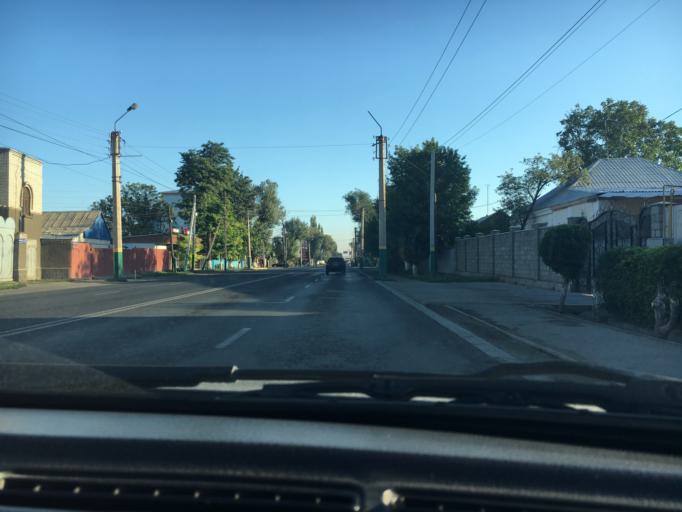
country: KZ
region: Zhambyl
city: Taraz
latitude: 42.8925
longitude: 71.3608
